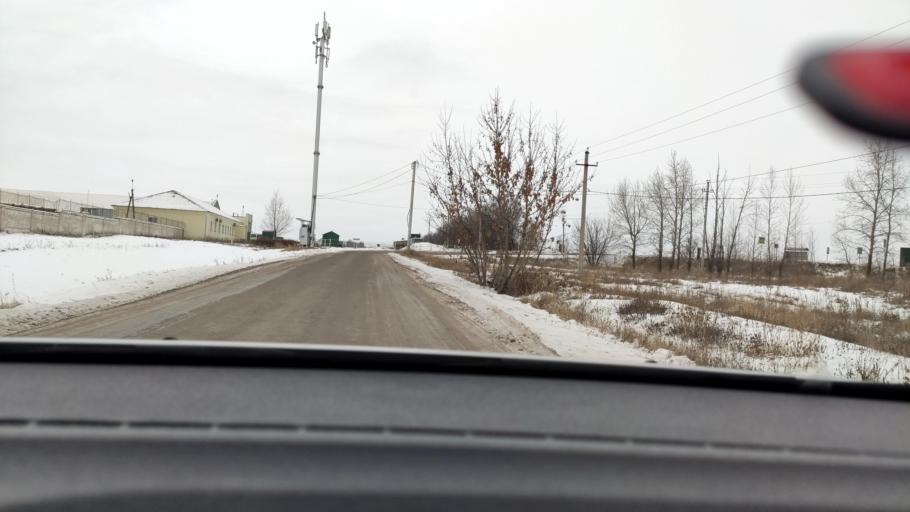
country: RU
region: Voronezj
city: Semiluki
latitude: 51.7223
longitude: 38.9954
